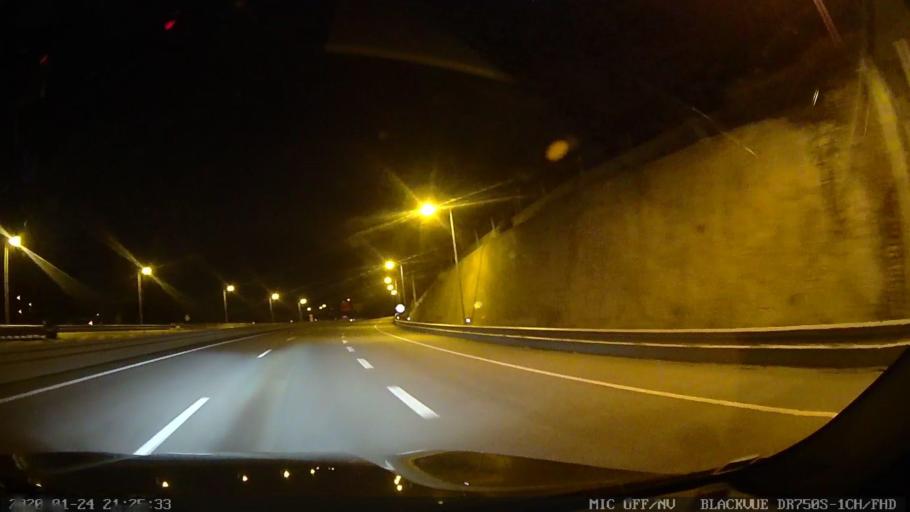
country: PT
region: Porto
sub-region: Amarante
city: Amarante
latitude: 41.2570
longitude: -8.0499
